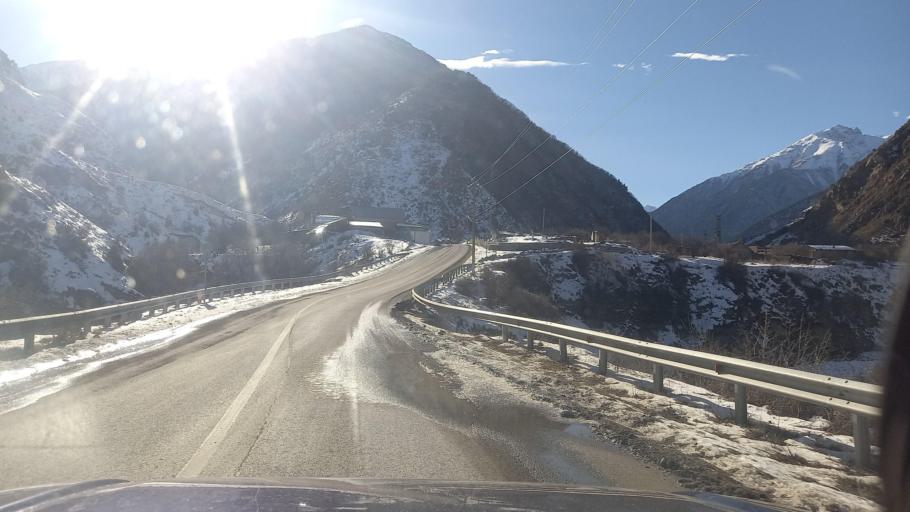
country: RU
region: North Ossetia
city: Chikola
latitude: 42.9838
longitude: 43.7780
